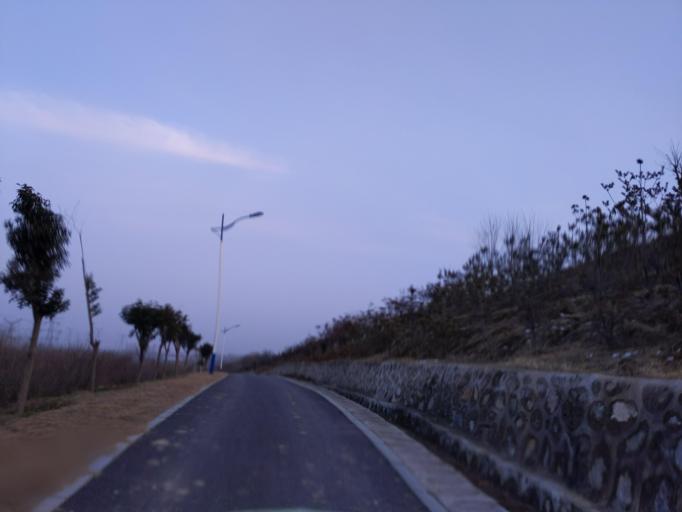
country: CN
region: Henan Sheng
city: Zhongyuanlu
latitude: 35.8162
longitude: 115.0573
